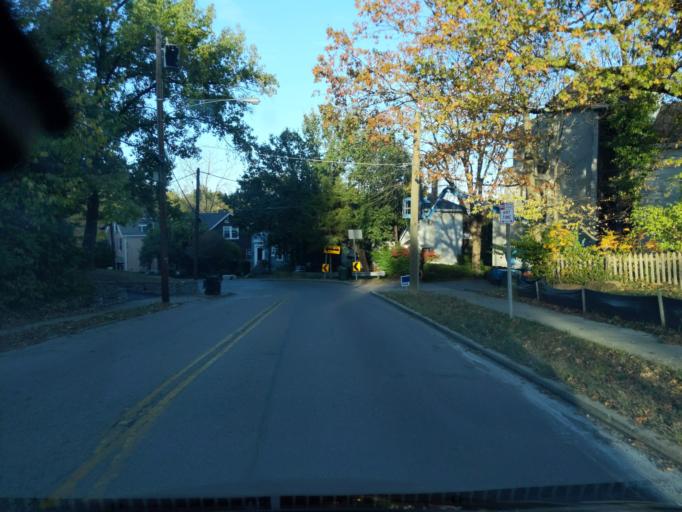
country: US
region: Kentucky
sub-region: Campbell County
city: Dayton
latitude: 39.1254
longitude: -84.4728
